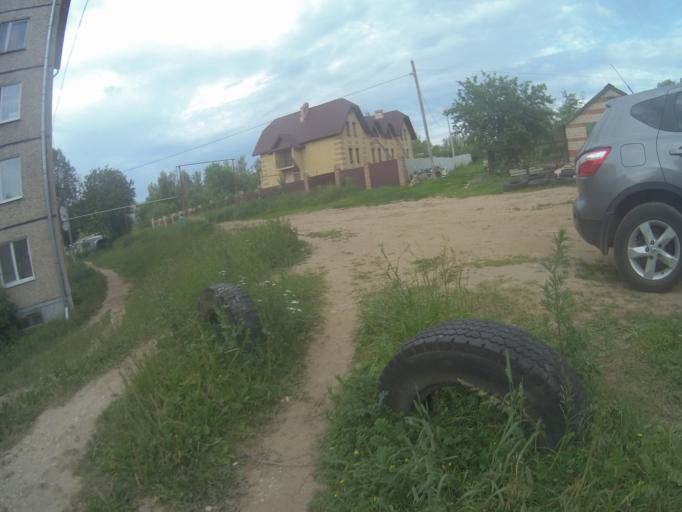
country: RU
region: Vladimir
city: Vladimir
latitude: 56.2199
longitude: 40.4084
